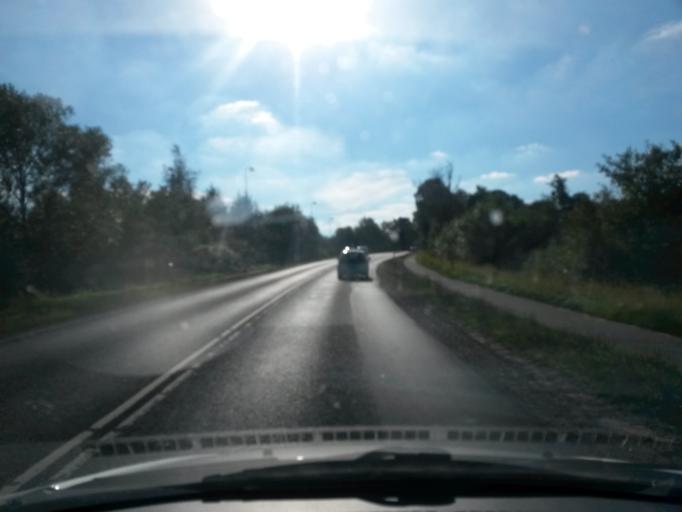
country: DK
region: Central Jutland
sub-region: Silkeborg Kommune
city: Silkeborg
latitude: 56.1537
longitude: 9.4980
